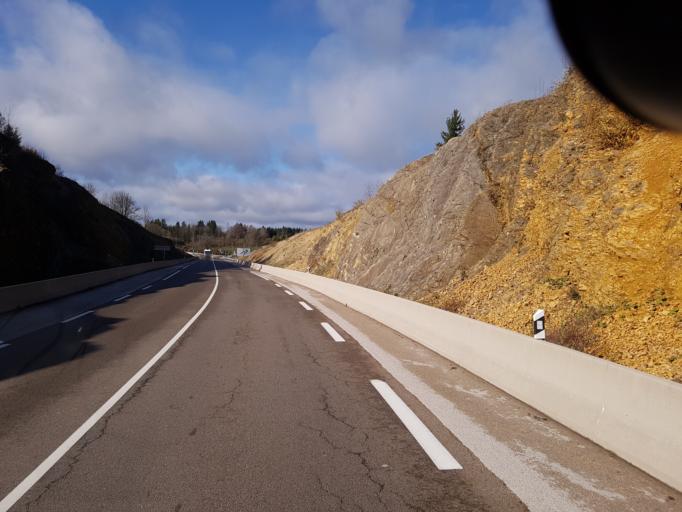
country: FR
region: Franche-Comte
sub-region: Departement du Jura
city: Morbier
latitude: 46.5830
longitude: 5.9572
